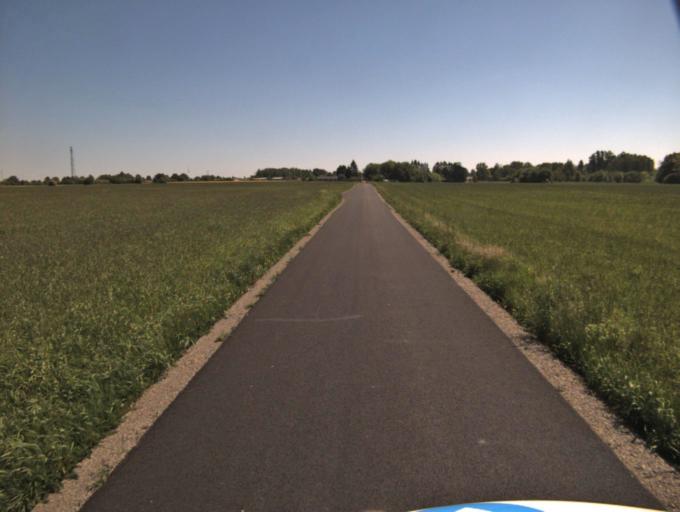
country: SE
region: Skane
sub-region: Kristianstads Kommun
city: Kristianstad
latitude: 56.0164
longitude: 14.2094
